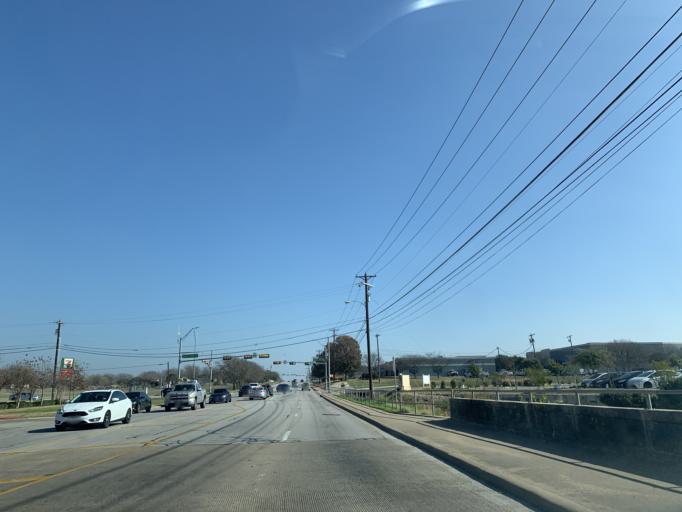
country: US
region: Texas
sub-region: Williamson County
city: Round Rock
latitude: 30.4963
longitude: -97.6465
